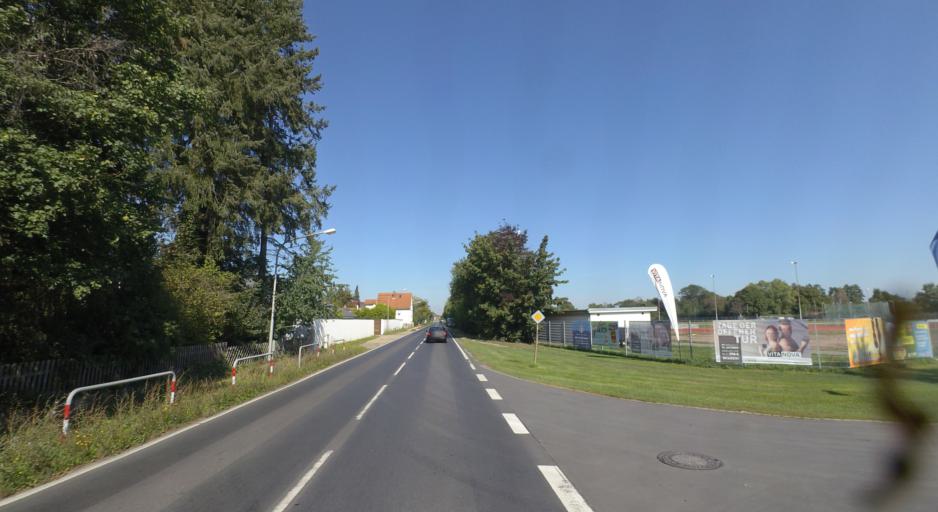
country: DE
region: Hesse
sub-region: Regierungsbezirk Darmstadt
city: Seligenstadt
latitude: 50.0328
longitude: 8.9851
